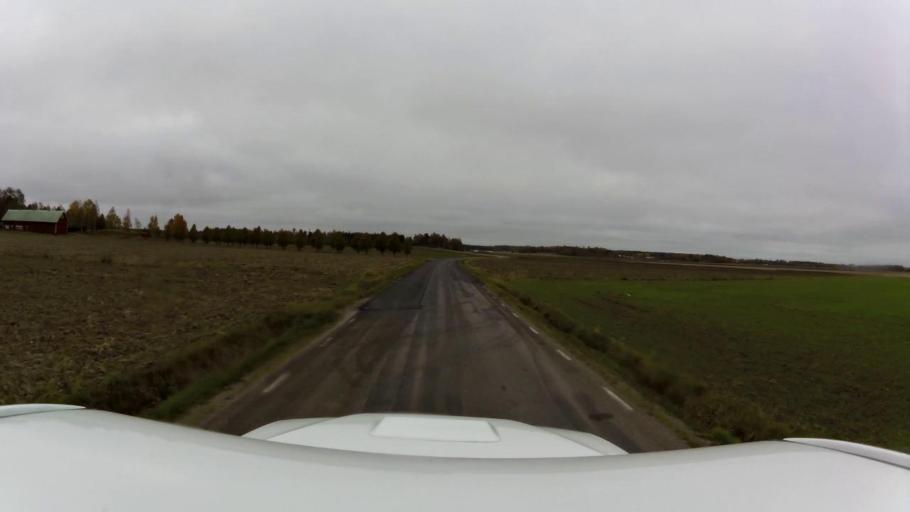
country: SE
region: OEstergoetland
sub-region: Linkopings Kommun
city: Linghem
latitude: 58.4476
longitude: 15.7112
